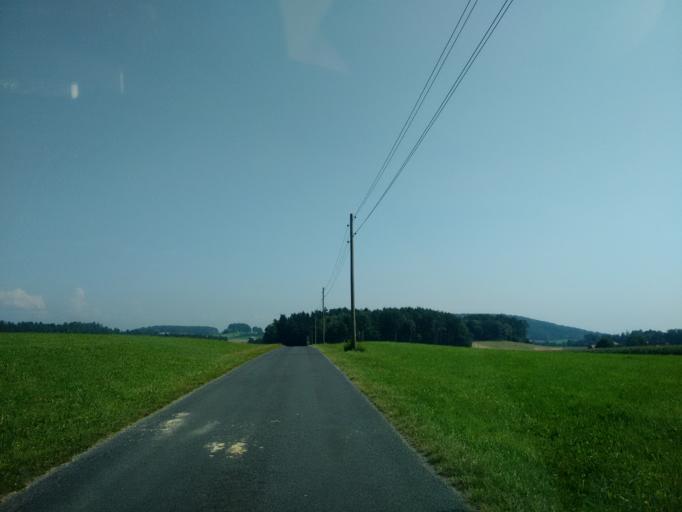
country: AT
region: Upper Austria
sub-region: Politischer Bezirk Urfahr-Umgebung
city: Haibach im Muhlkreis
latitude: 48.4112
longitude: 14.3521
